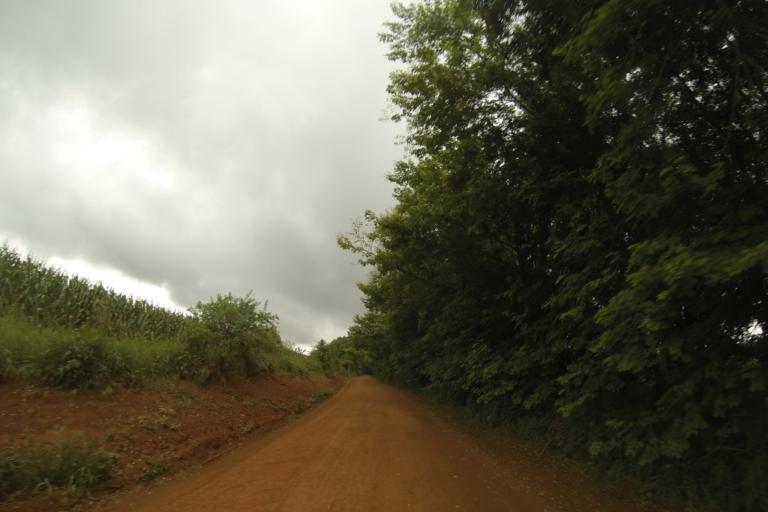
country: BR
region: Minas Gerais
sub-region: Campos Altos
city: Campos Altos
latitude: -19.8185
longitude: -46.3319
